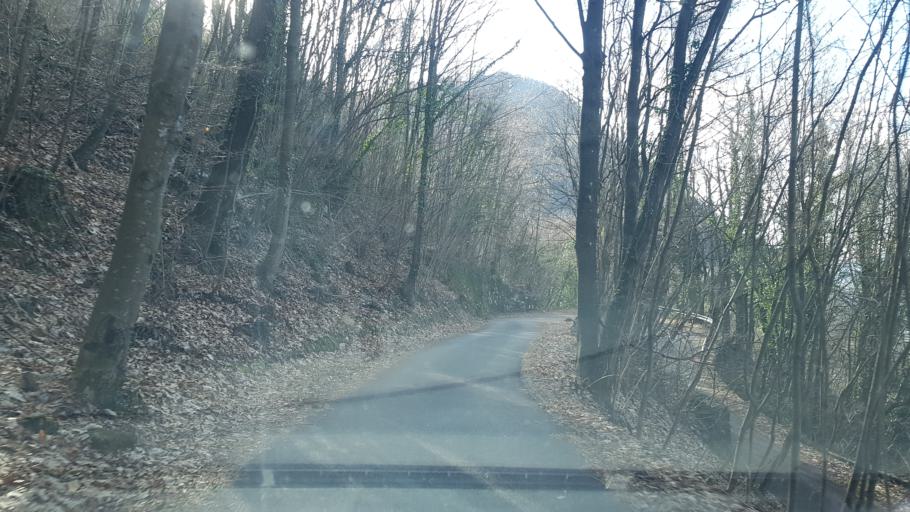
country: IT
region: Friuli Venezia Giulia
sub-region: Provincia di Udine
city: Gemona
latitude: 46.2841
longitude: 13.1561
